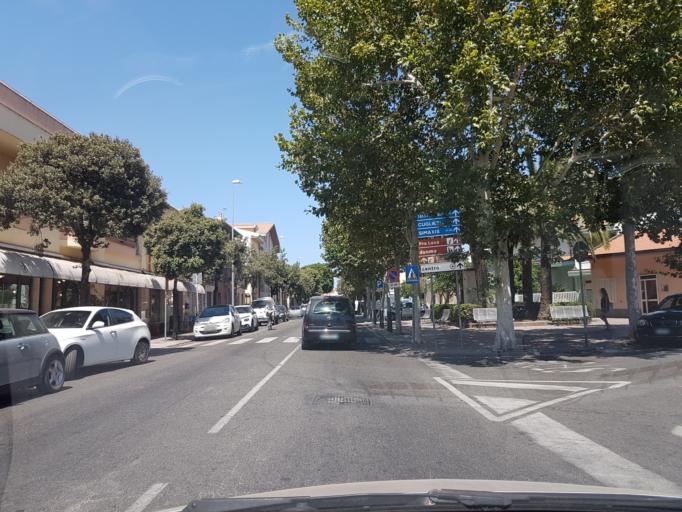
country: IT
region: Sardinia
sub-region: Provincia di Oristano
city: Oristano
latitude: 39.8971
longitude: 8.5951
